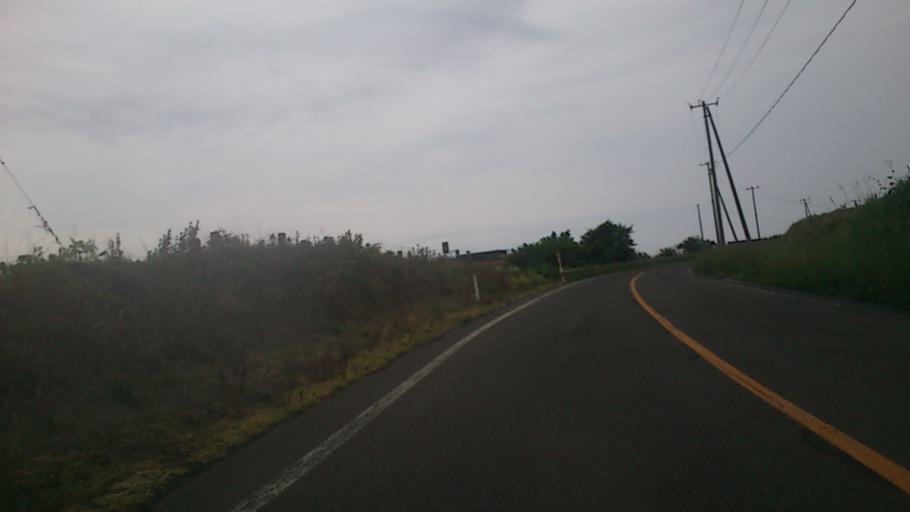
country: JP
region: Akita
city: Noshiromachi
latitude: 40.3776
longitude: 140.0078
